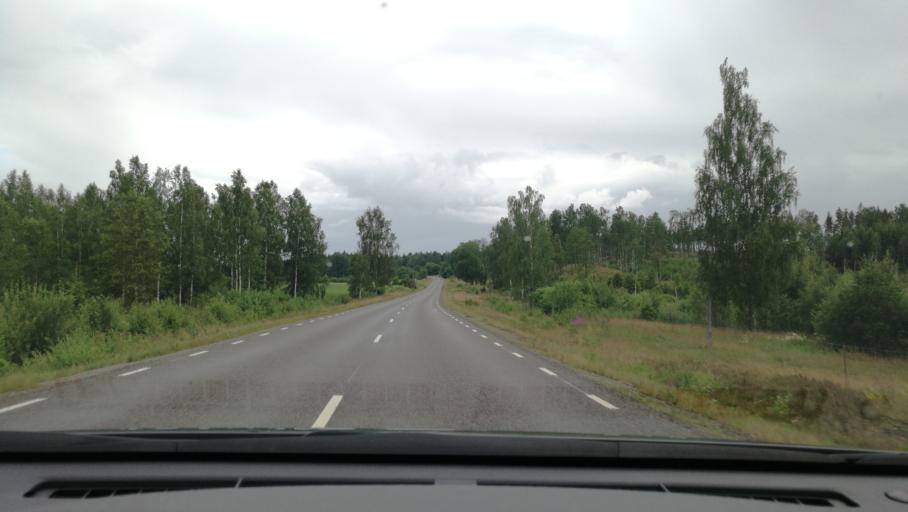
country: SE
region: OEstergoetland
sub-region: Norrkopings Kommun
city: Svartinge
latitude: 58.7806
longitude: 15.9667
